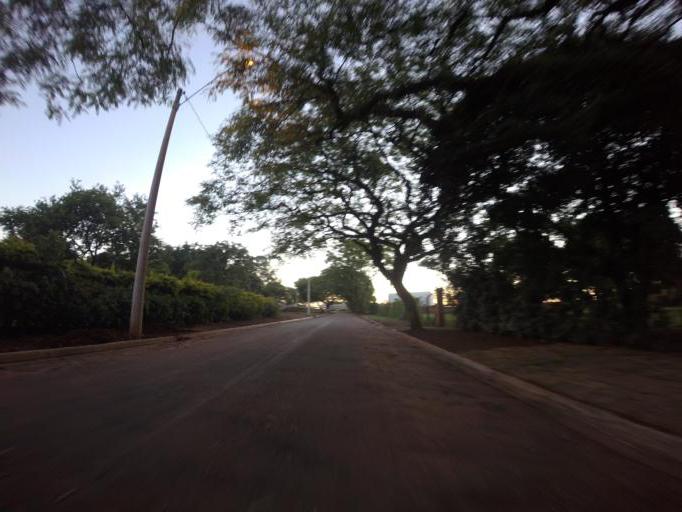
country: BR
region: Sao Paulo
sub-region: Piracicaba
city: Piracicaba
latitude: -22.7556
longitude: -47.5959
